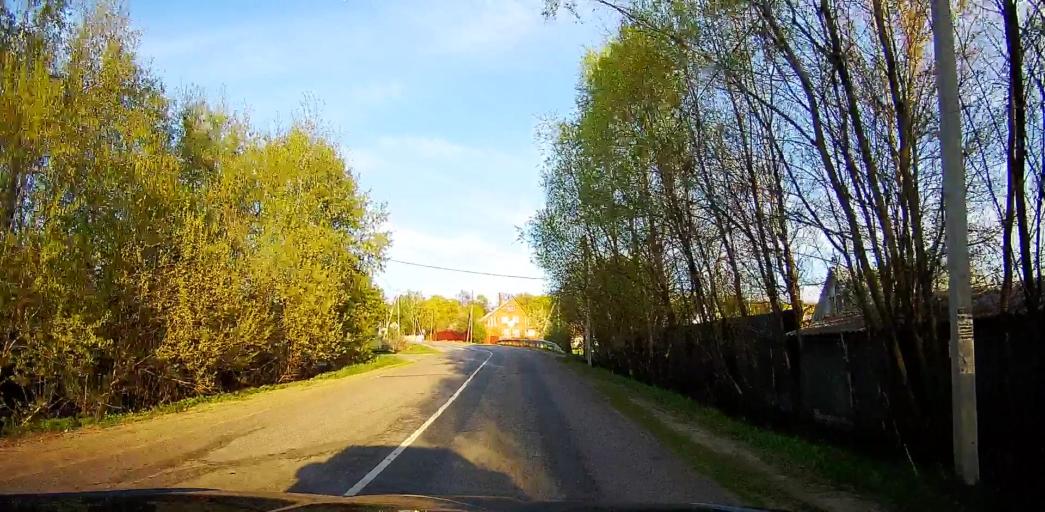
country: RU
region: Moskovskaya
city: Meshcherino
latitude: 55.2438
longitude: 38.3125
